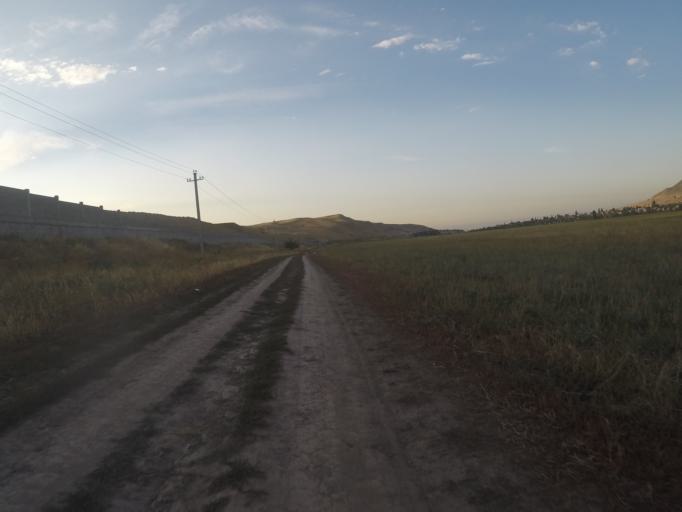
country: KG
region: Chuy
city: Bishkek
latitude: 42.7544
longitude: 74.6366
